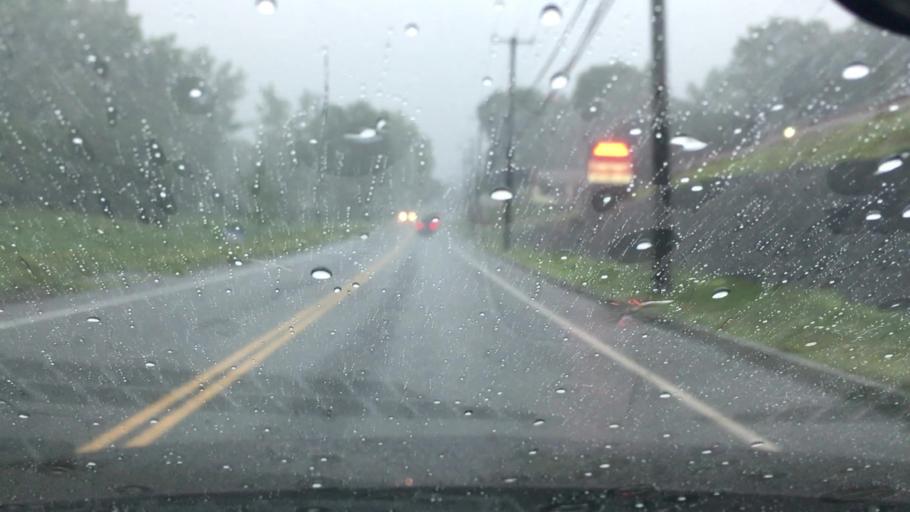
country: US
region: Connecticut
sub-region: Hartford County
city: Manchester
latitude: 41.7952
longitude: -72.5349
